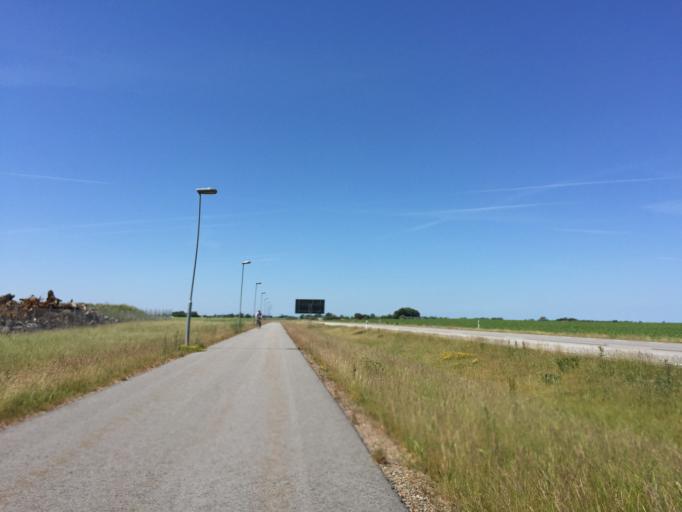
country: SE
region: Skane
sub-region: Trelleborgs Kommun
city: Trelleborg
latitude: 55.3871
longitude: 13.1074
